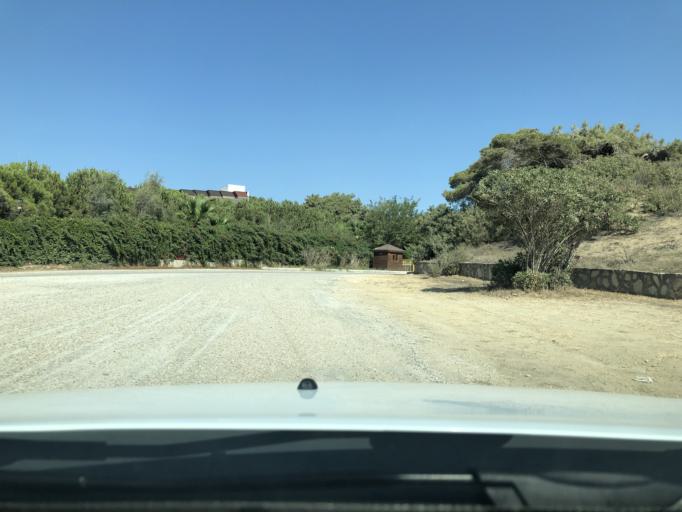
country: TR
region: Antalya
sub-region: Manavgat
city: Manavgat
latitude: 36.7575
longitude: 31.4232
